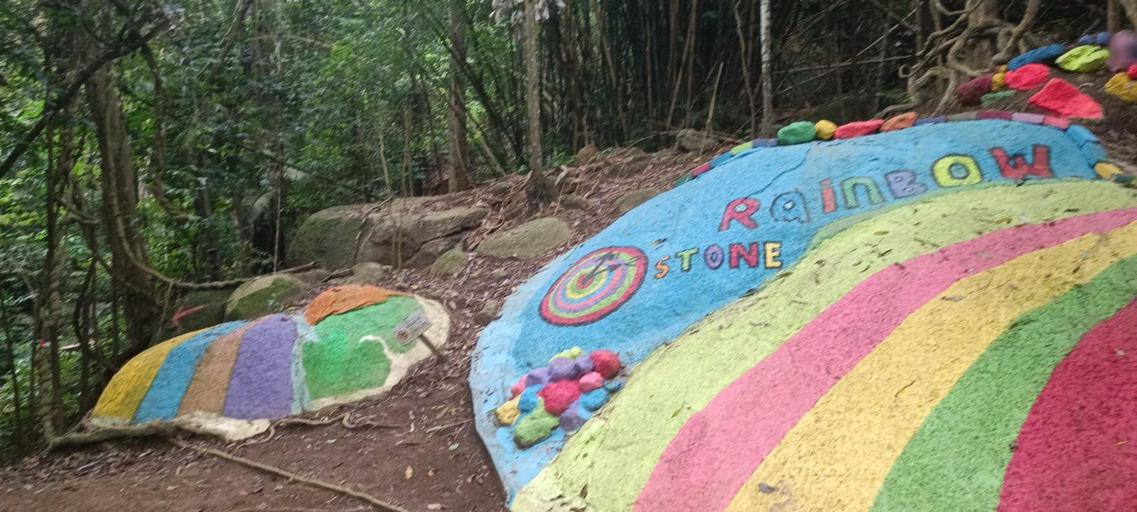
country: MY
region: Penang
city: Kampung Sungai Ara
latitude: 5.2611
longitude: 100.2761
